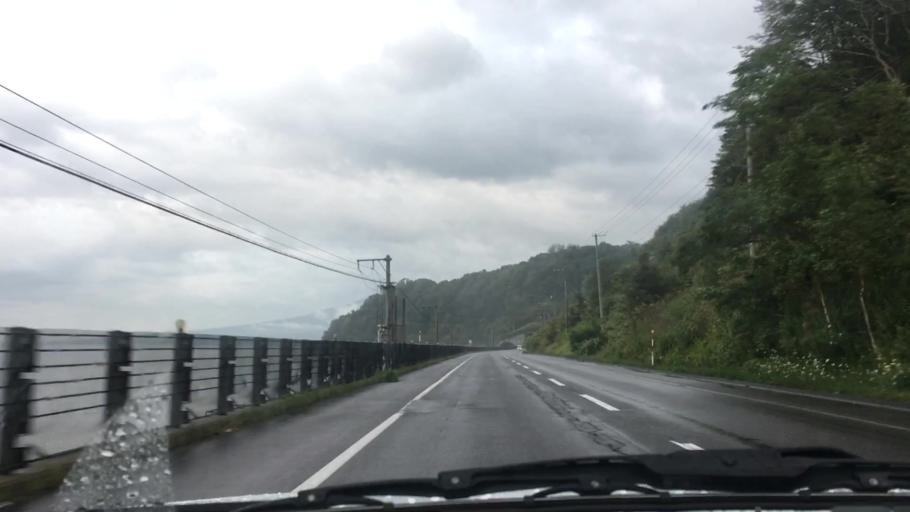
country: JP
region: Hokkaido
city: Nanae
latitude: 42.1237
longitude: 140.5247
